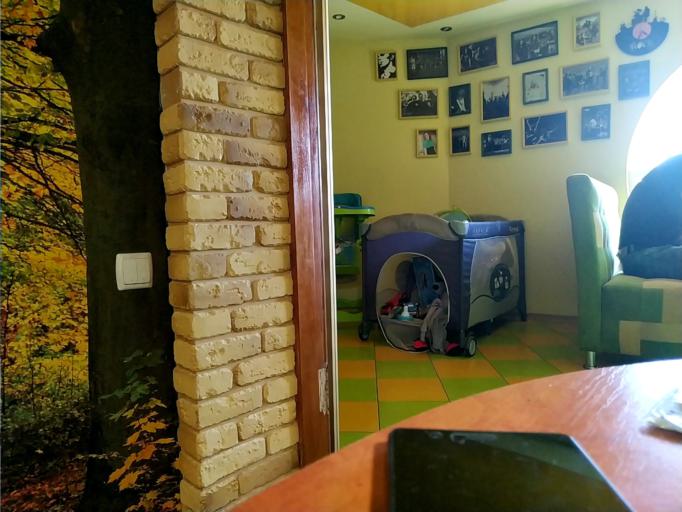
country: RU
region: Rjazan
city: Putyatino
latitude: 53.9601
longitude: 41.2993
